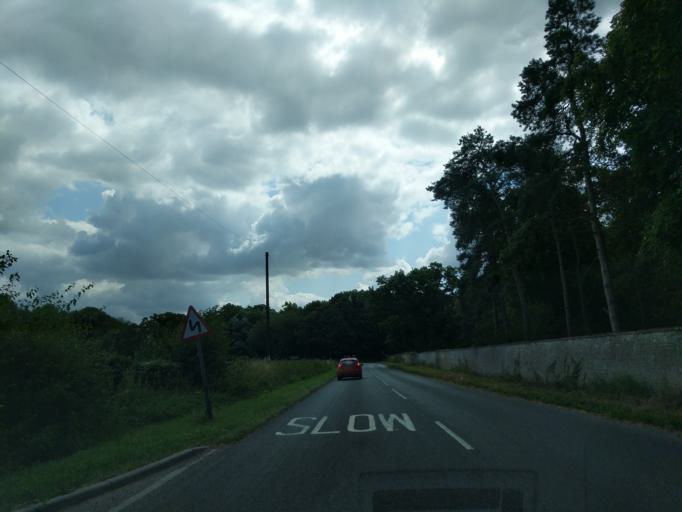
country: GB
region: England
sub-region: Cambridgeshire
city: Isleham
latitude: 52.2941
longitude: 0.4494
